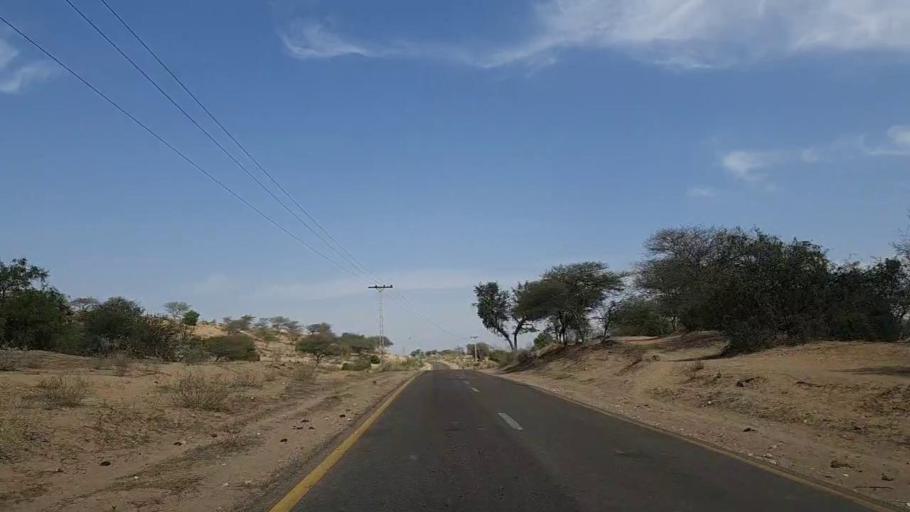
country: PK
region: Sindh
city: Mithi
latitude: 24.8396
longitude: 69.8347
